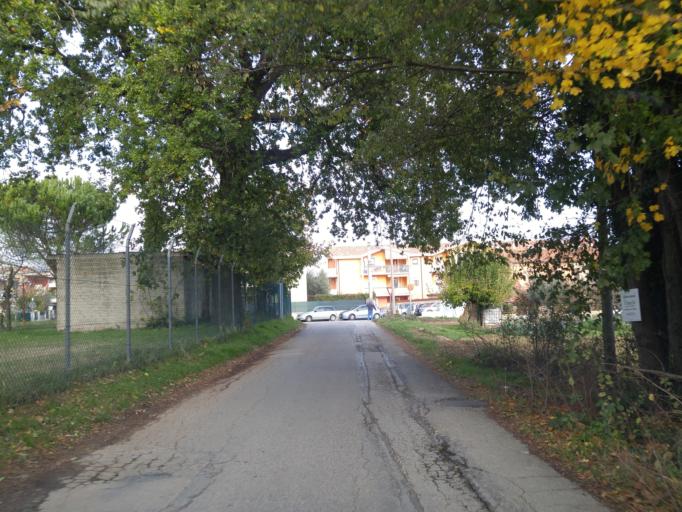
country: IT
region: The Marches
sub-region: Provincia di Pesaro e Urbino
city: Lucrezia
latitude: 43.7806
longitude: 12.9397
